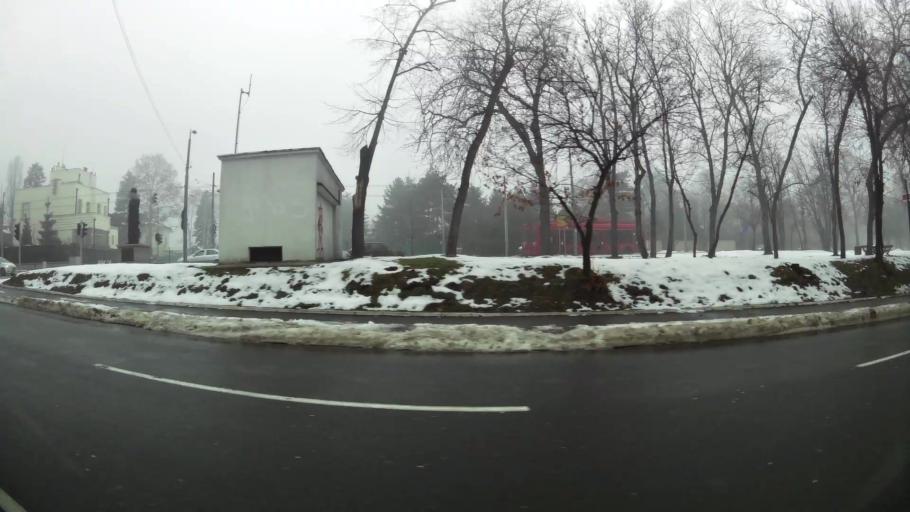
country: RS
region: Central Serbia
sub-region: Belgrade
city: Savski Venac
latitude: 44.7795
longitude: 20.4587
